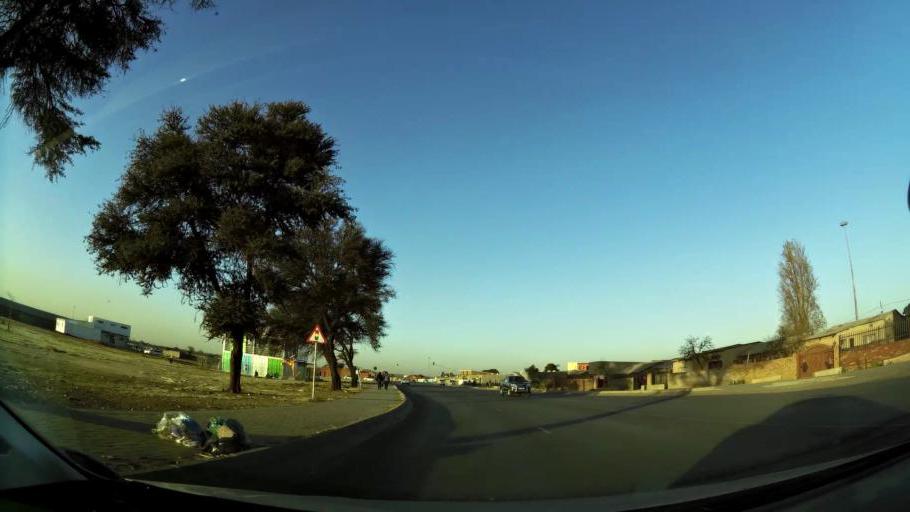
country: ZA
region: Gauteng
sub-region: Ekurhuleni Metropolitan Municipality
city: Tembisa
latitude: -26.0010
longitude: 28.2304
